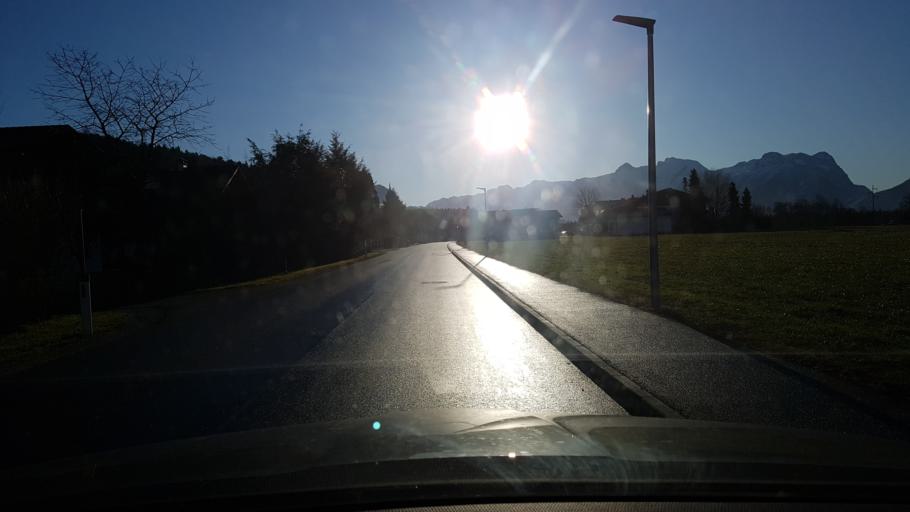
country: AT
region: Salzburg
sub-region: Politischer Bezirk Hallein
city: Adnet
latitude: 47.6653
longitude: 13.1367
